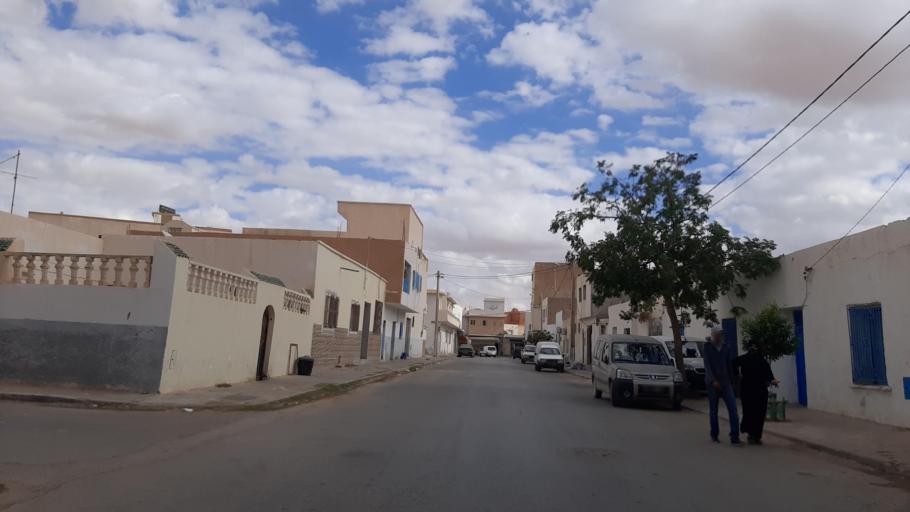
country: TN
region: Tataouine
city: Tataouine
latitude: 32.9320
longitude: 10.4490
